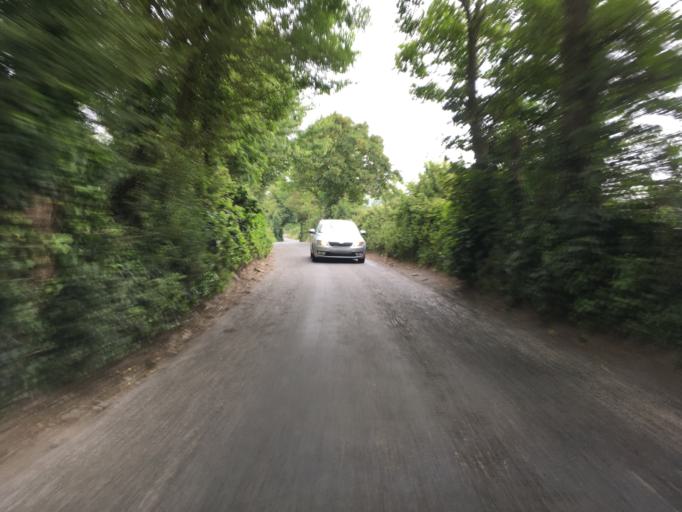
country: GB
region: England
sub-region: North Somerset
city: Yatton
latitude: 51.4184
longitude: -2.8009
